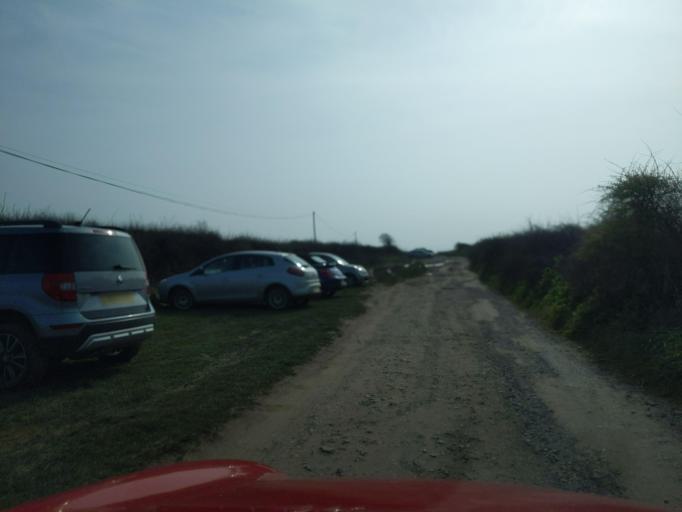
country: GB
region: England
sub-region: Devon
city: Salcombe
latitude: 50.2234
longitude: -3.7502
